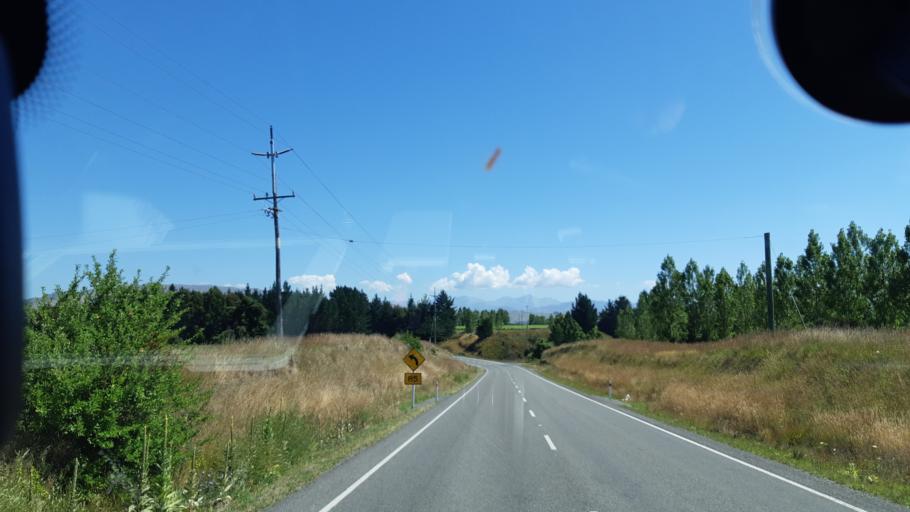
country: NZ
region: Canterbury
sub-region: Kaikoura District
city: Kaikoura
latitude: -42.7542
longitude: 173.2735
